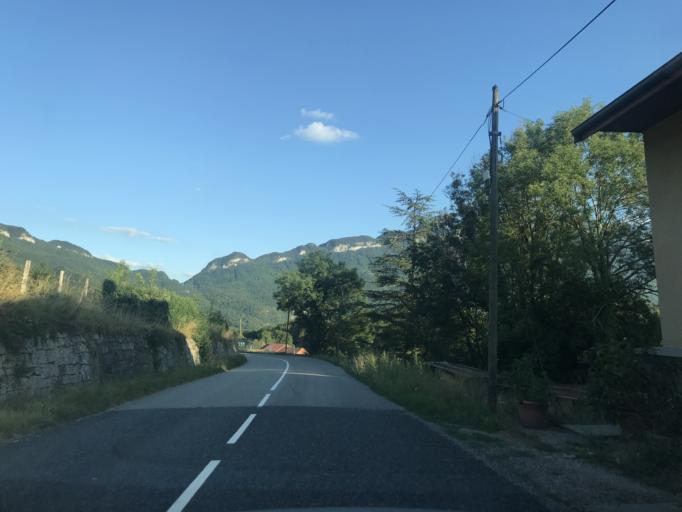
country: FR
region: Rhone-Alpes
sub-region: Departement de la Savoie
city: Yenne
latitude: 45.7168
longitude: 5.8124
